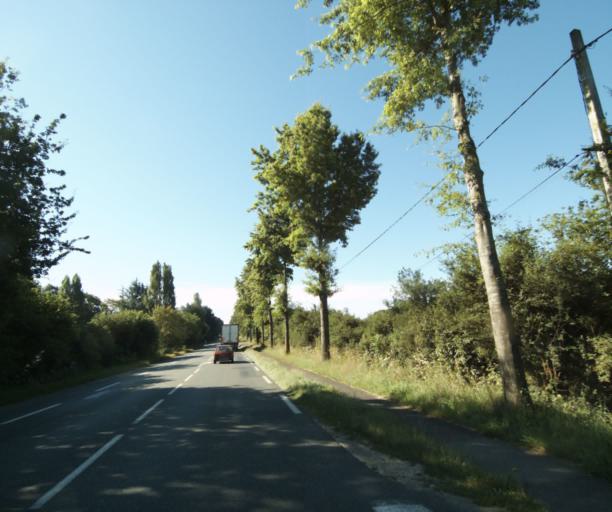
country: FR
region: Pays de la Loire
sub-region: Departement de la Mayenne
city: Laval
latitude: 48.0421
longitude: -0.7425
